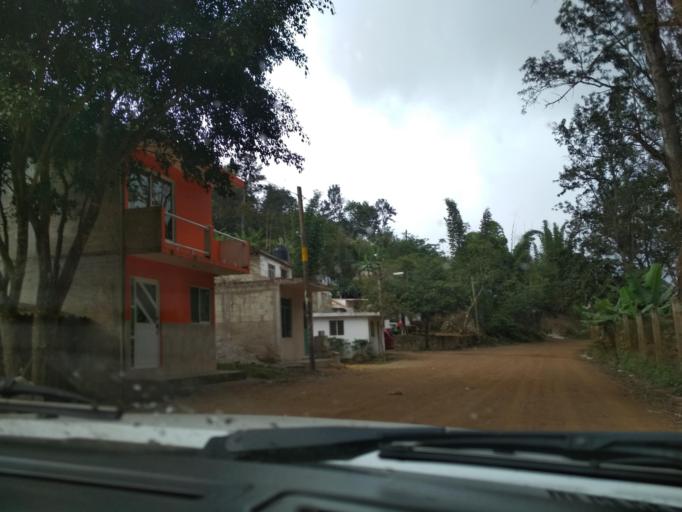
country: MX
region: Veracruz
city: El Castillo
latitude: 19.5438
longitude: -96.8352
